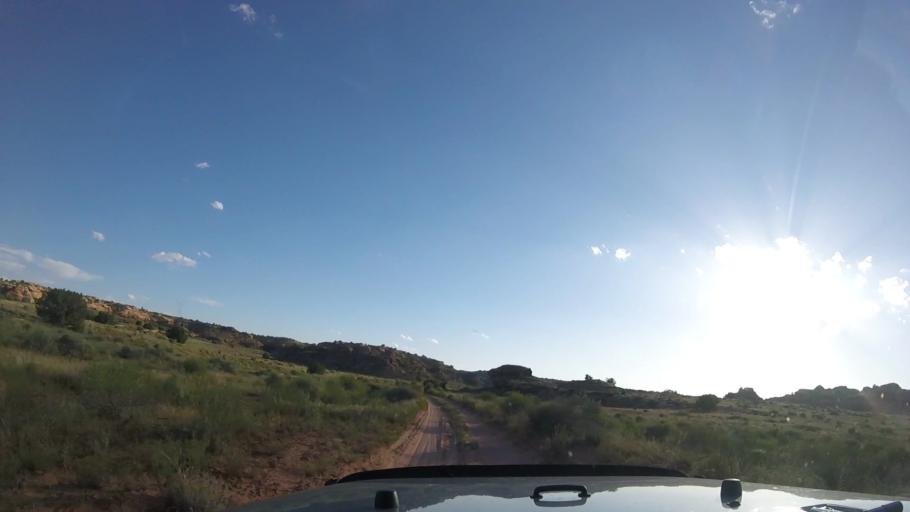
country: US
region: Utah
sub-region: Grand County
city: Moab
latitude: 38.1960
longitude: -109.7834
